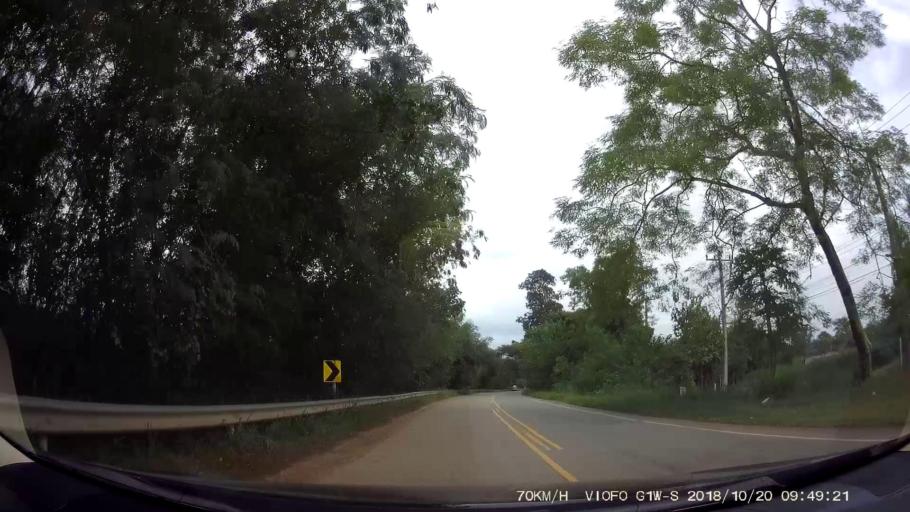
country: TH
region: Chaiyaphum
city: Khon San
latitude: 16.5185
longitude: 101.9055
